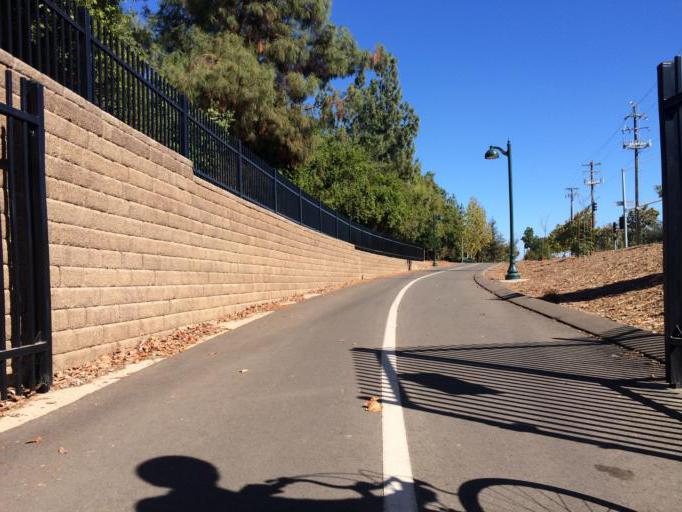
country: US
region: California
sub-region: Fresno County
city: Clovis
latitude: 36.8667
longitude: -119.7668
